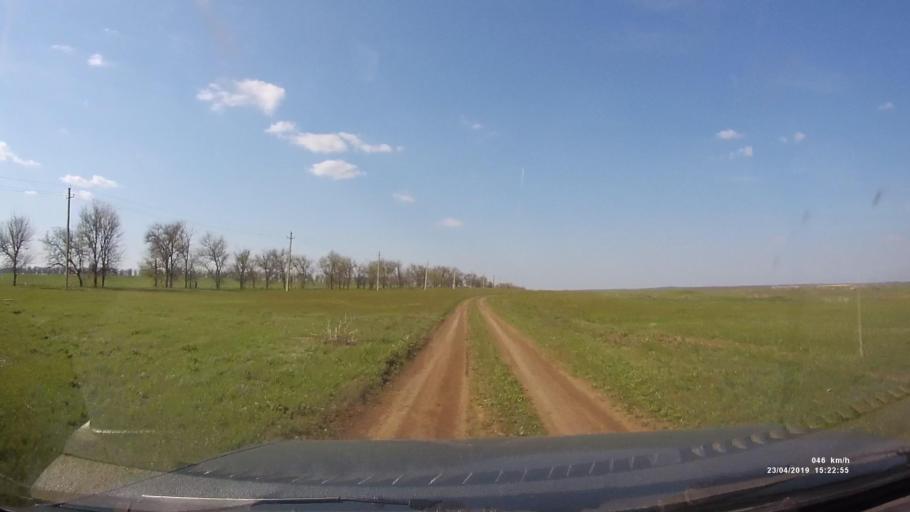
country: RU
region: Rostov
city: Remontnoye
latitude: 46.5318
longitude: 42.9697
